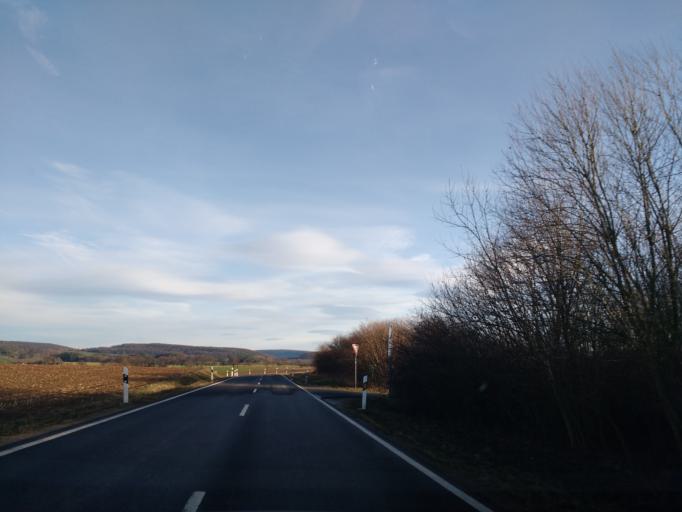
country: DE
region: Thuringia
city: Burgwalde
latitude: 51.3885
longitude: 10.0295
